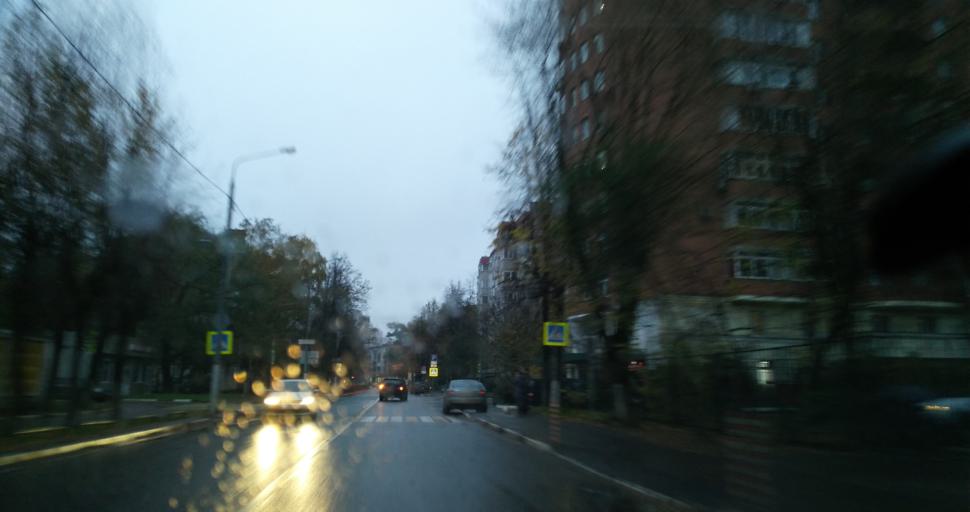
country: RU
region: Moscow
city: Khimki
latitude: 55.8942
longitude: 37.4382
